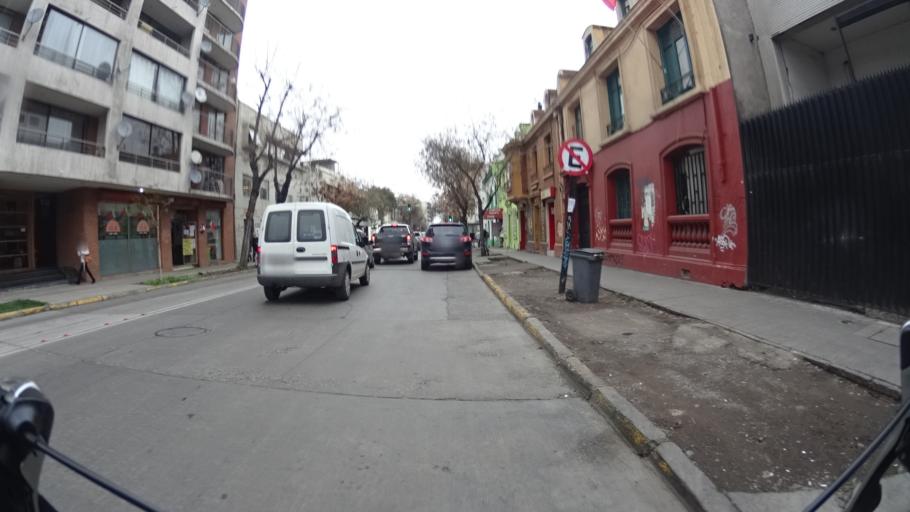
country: CL
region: Santiago Metropolitan
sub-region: Provincia de Santiago
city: Santiago
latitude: -33.4494
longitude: -70.6602
